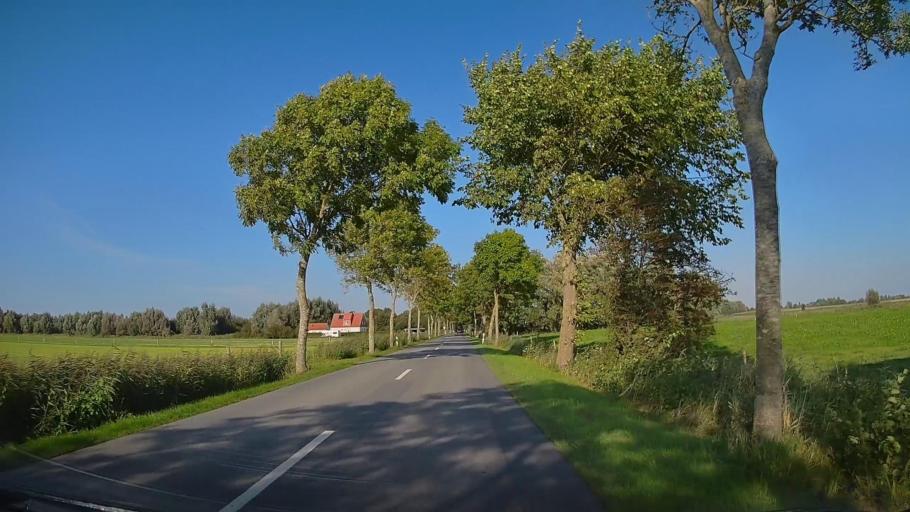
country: DE
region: Lower Saxony
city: Padingbuttel
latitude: 53.7325
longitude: 8.5451
